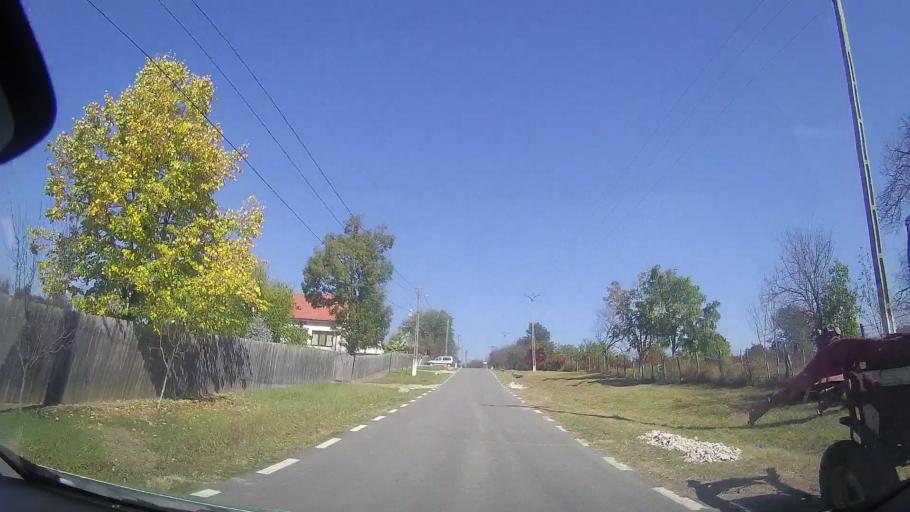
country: RO
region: Timis
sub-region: Comuna Ohaba Lunga
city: Ohaba Lunga
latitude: 45.9055
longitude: 21.9367
